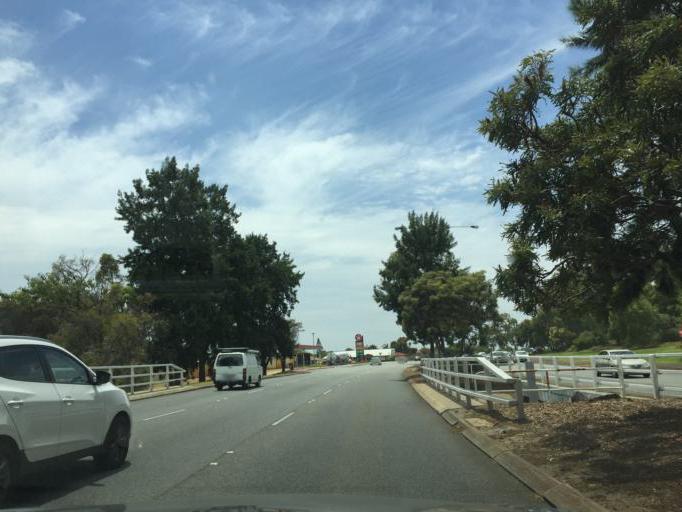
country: AU
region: Western Australia
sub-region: Melville
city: Winthrop
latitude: -32.0638
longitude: 115.8341
